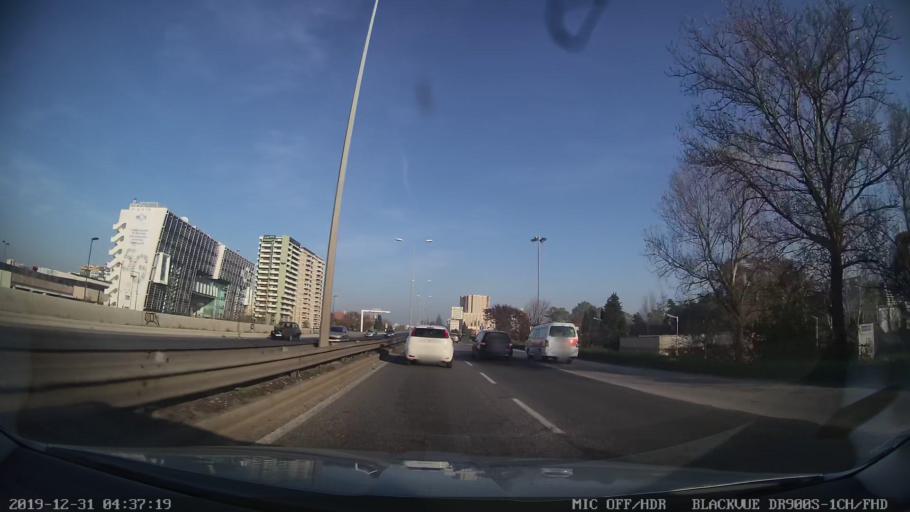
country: PT
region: Lisbon
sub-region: Odivelas
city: Olival do Basto
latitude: 38.7577
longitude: -9.1589
